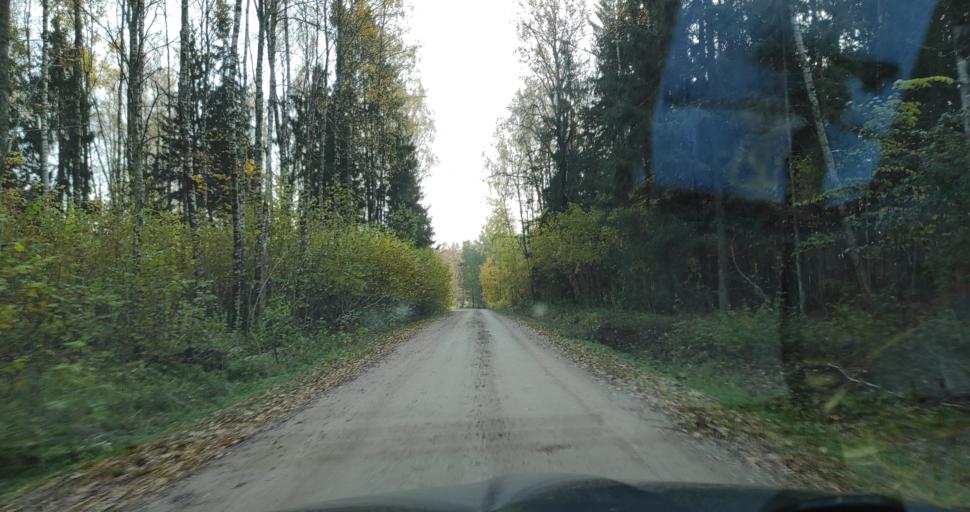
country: LV
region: Vainode
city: Vainode
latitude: 56.4271
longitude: 21.8736
